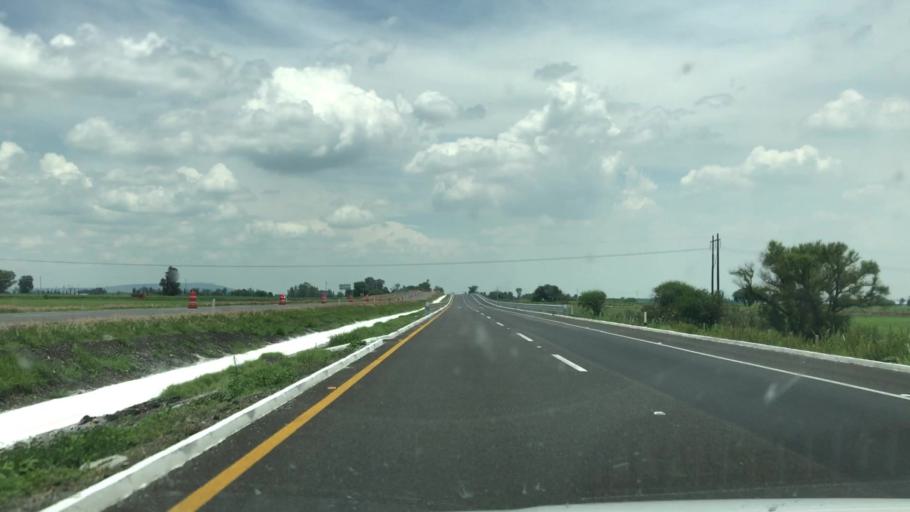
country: MX
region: Guanajuato
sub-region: Irapuato
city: Cuarta Brigada
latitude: 20.6474
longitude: -101.2776
